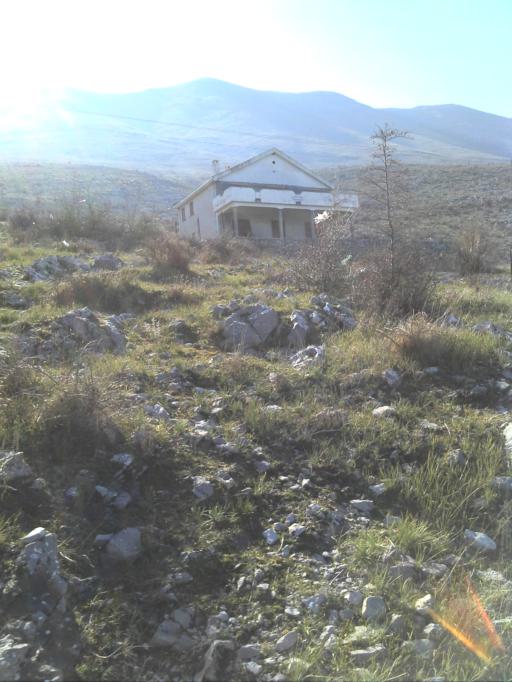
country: AL
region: Shkoder
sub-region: Rrethi i Shkodres
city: Berdica e Madhe
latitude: 42.0624
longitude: 19.4411
